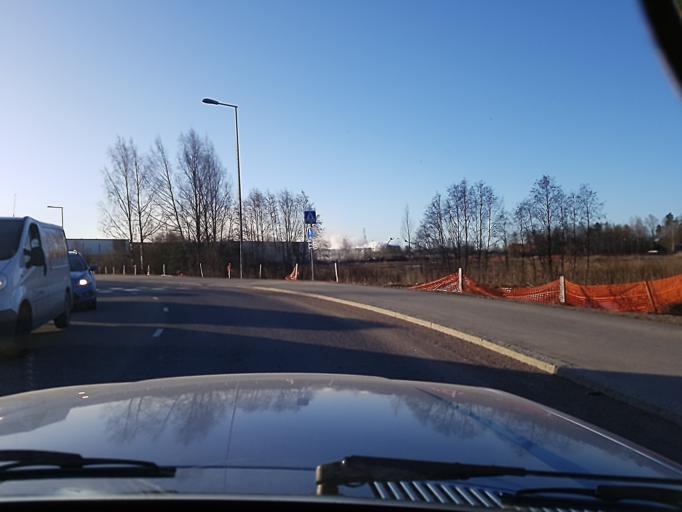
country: FI
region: Uusimaa
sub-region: Helsinki
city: Vantaa
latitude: 60.2957
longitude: 24.9763
